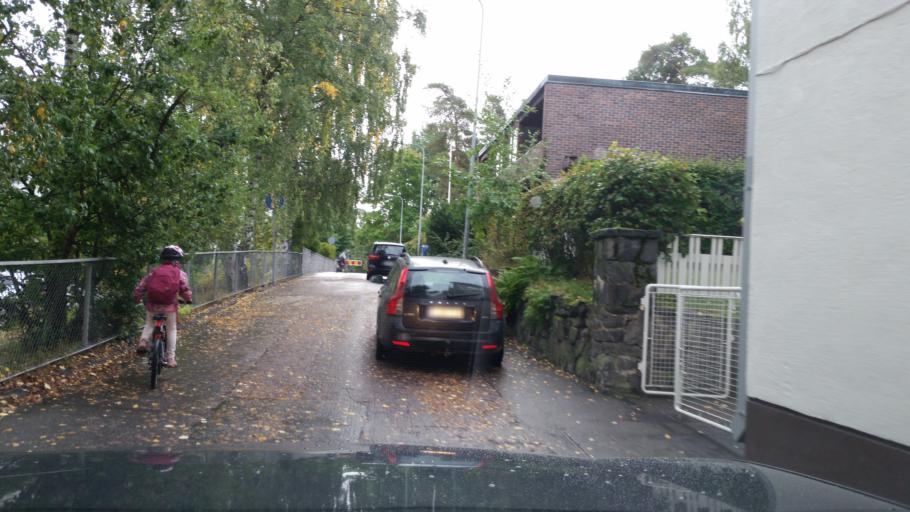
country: FI
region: Uusimaa
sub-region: Helsinki
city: Teekkarikylae
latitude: 60.1991
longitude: 24.8692
